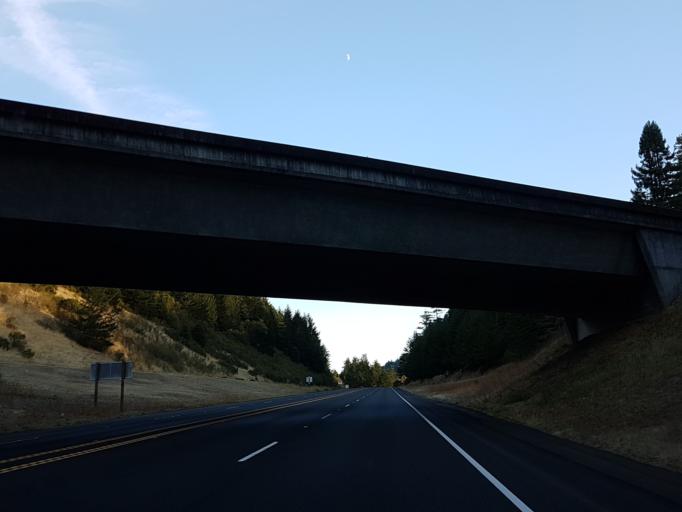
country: US
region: California
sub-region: Humboldt County
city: Redway
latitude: 39.9444
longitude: -123.7795
